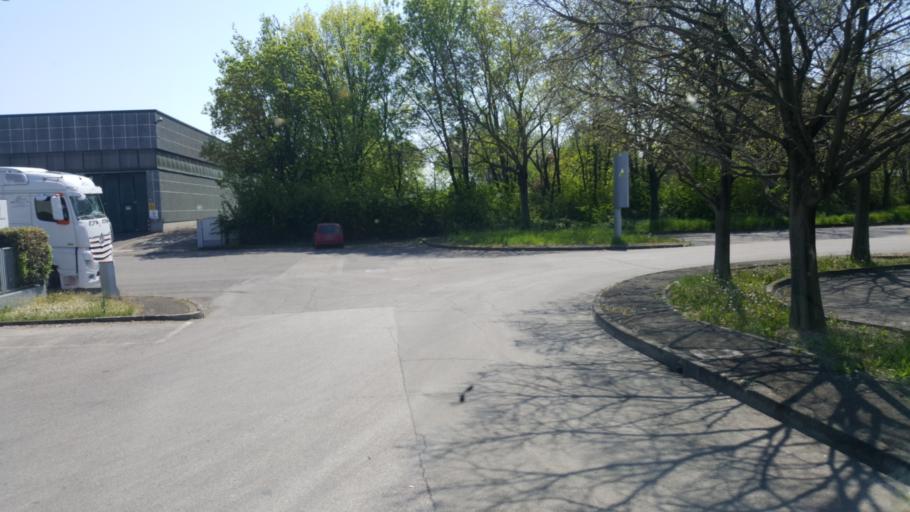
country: IT
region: Emilia-Romagna
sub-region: Provincia di Reggio Emilia
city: Bagnolo in Piano
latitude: 44.7354
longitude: 10.6561
